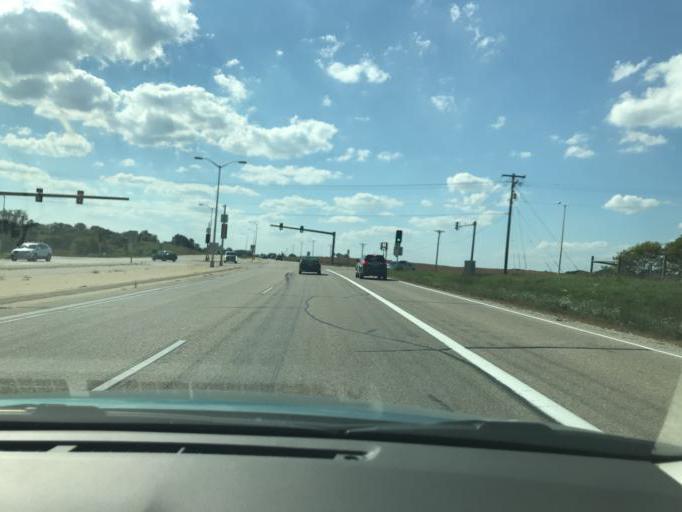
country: US
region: Wisconsin
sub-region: Kenosha County
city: Powers Lake
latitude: 42.5836
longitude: -88.2949
